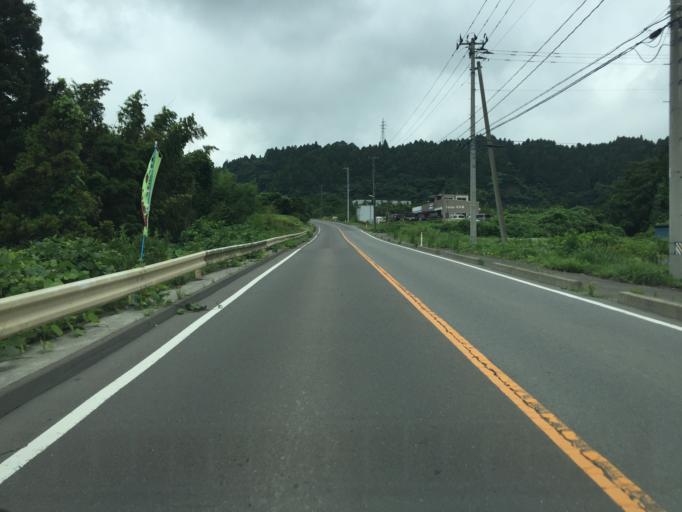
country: JP
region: Miyagi
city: Watari
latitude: 38.0322
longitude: 140.8354
